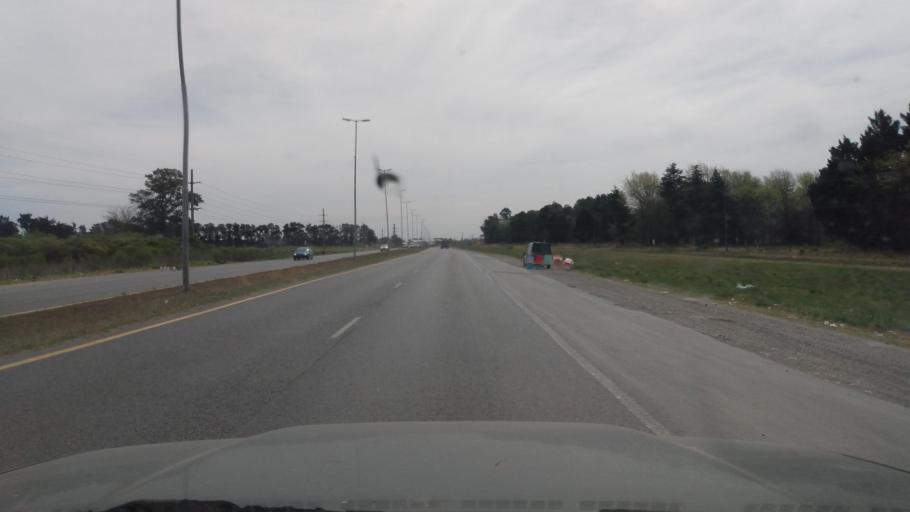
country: AR
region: Buenos Aires
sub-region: Partido de Lujan
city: Lujan
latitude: -34.5657
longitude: -59.0368
